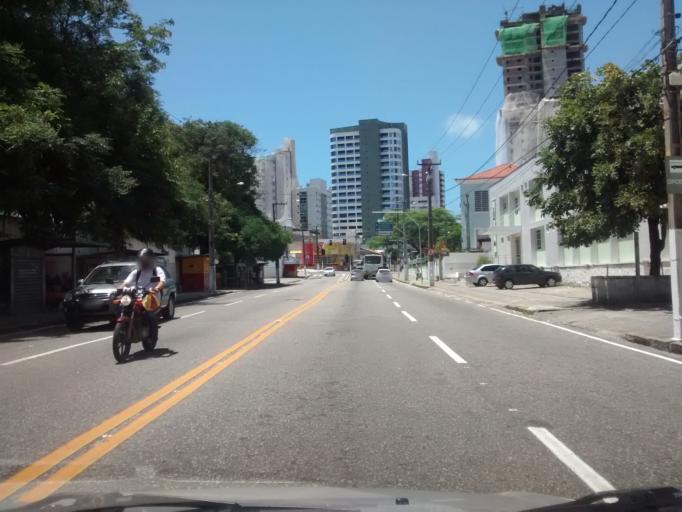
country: BR
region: Rio Grande do Norte
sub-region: Natal
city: Natal
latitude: -5.7809
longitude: -35.1984
